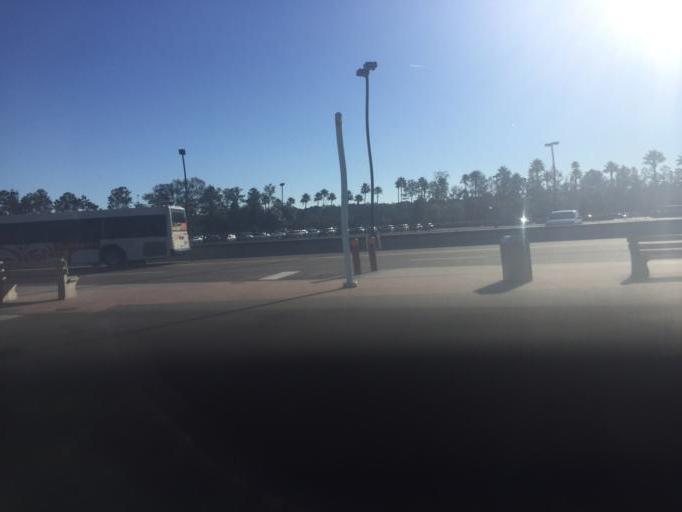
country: US
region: Florida
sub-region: Osceola County
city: Celebration
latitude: 28.3589
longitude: -81.5565
